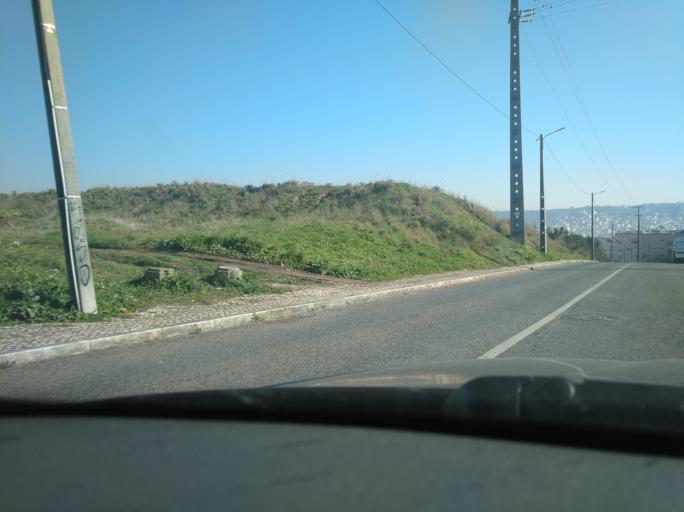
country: PT
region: Lisbon
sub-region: Odivelas
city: Famoes
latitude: 38.7820
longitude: -9.2117
